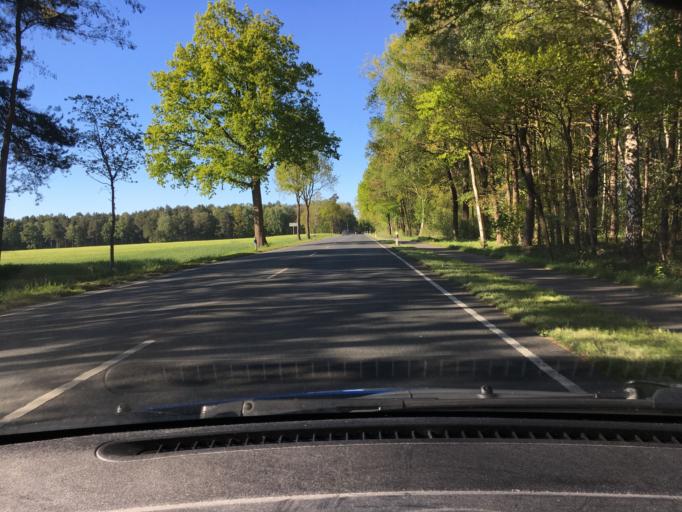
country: DE
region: Lower Saxony
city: Soltau
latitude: 53.0411
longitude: 9.8553
